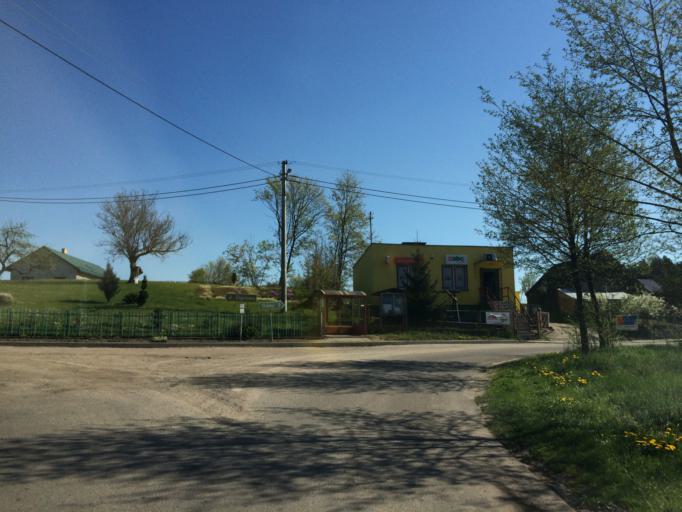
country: PL
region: Warmian-Masurian Voivodeship
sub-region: Powiat dzialdowski
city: Rybno
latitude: 53.4440
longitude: 19.9245
